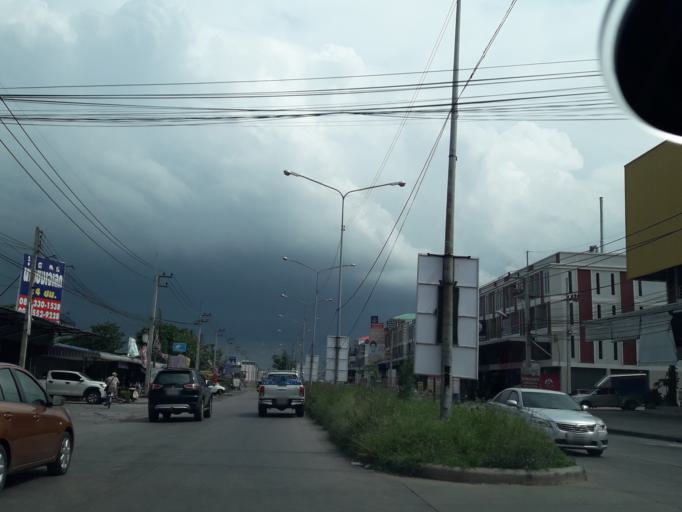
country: TH
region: Pathum Thani
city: Khlong Luang
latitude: 14.0788
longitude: 100.6339
